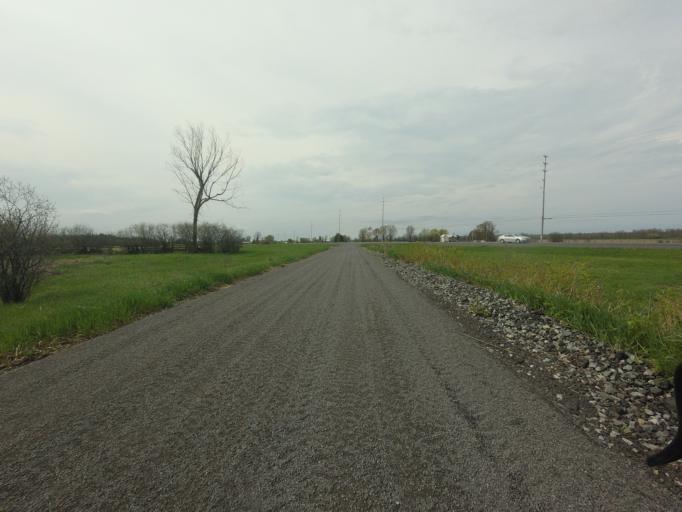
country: CA
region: Ontario
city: Carleton Place
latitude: 45.1828
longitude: -76.1578
